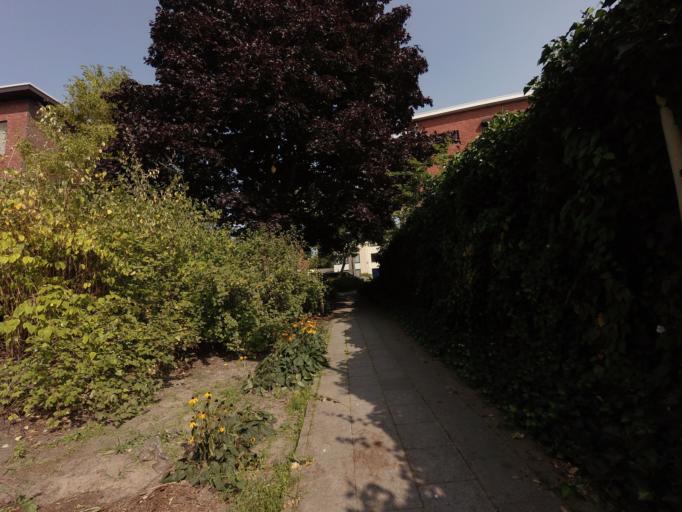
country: BE
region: Flanders
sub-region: Provincie Antwerpen
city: Aartselaar
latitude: 51.1536
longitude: 4.3914
